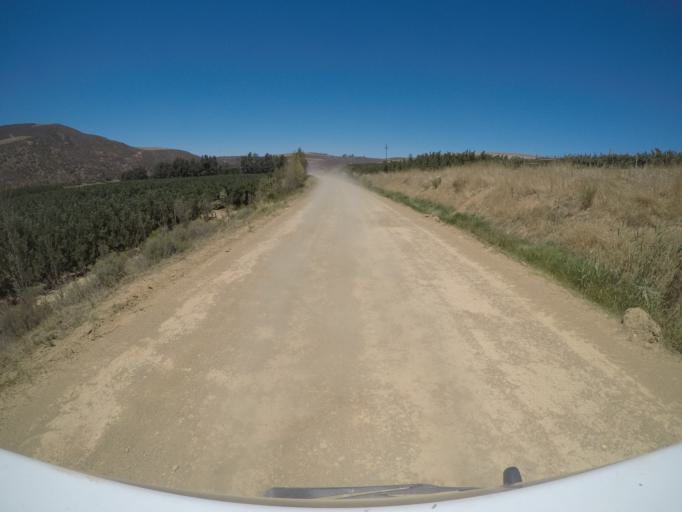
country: ZA
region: Western Cape
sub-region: Overberg District Municipality
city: Grabouw
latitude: -34.1088
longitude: 19.2119
